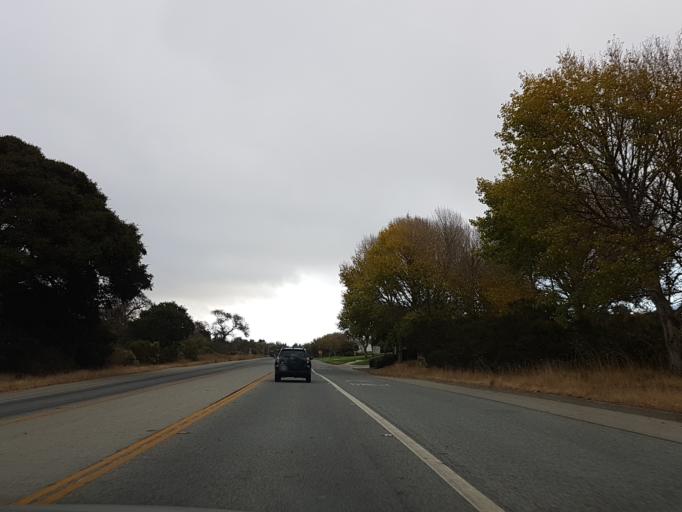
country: US
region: California
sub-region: Monterey County
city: Salinas
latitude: 36.6097
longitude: -121.6507
